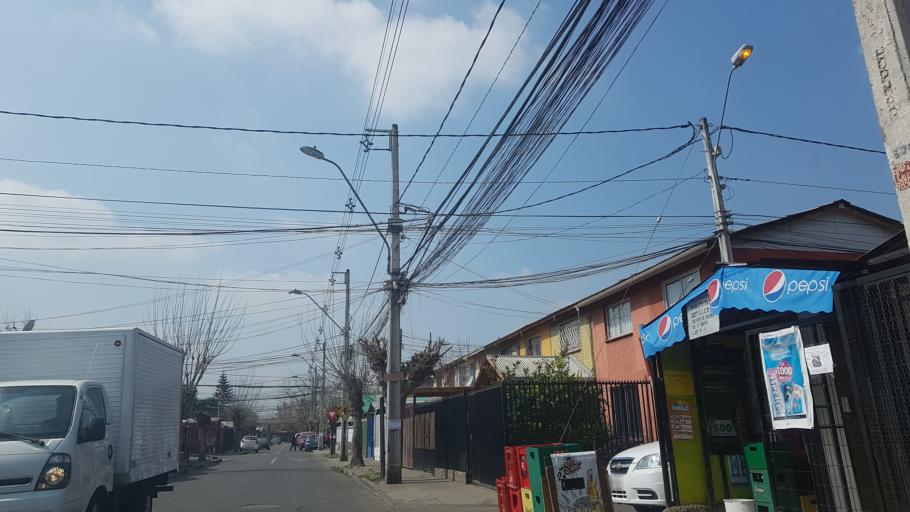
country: CL
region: Santiago Metropolitan
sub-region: Provincia de Santiago
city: Lo Prado
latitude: -33.3596
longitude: -70.7175
